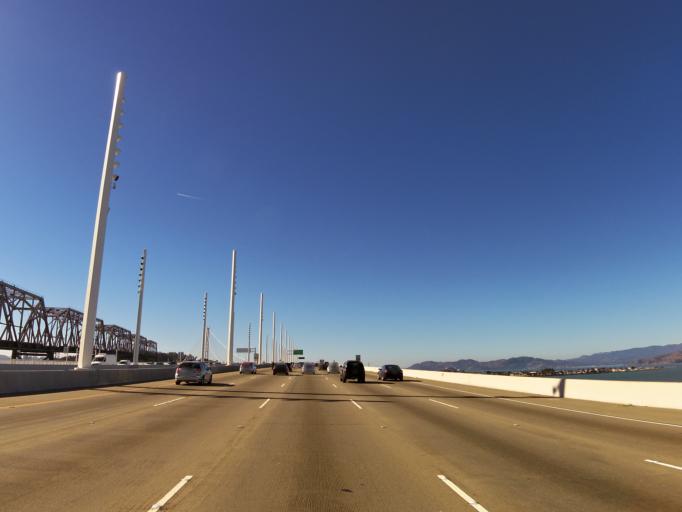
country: US
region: California
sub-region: Alameda County
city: Emeryville
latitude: 37.8201
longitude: -122.3430
